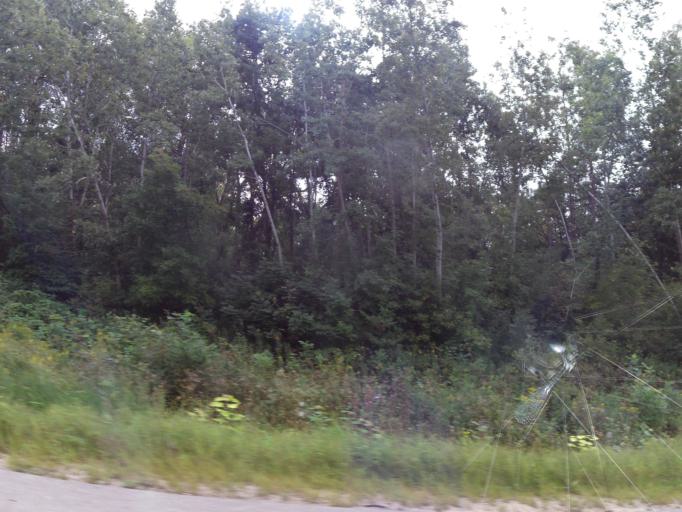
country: US
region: Wisconsin
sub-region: La Crosse County
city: West Salem
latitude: 43.8835
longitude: -91.1136
